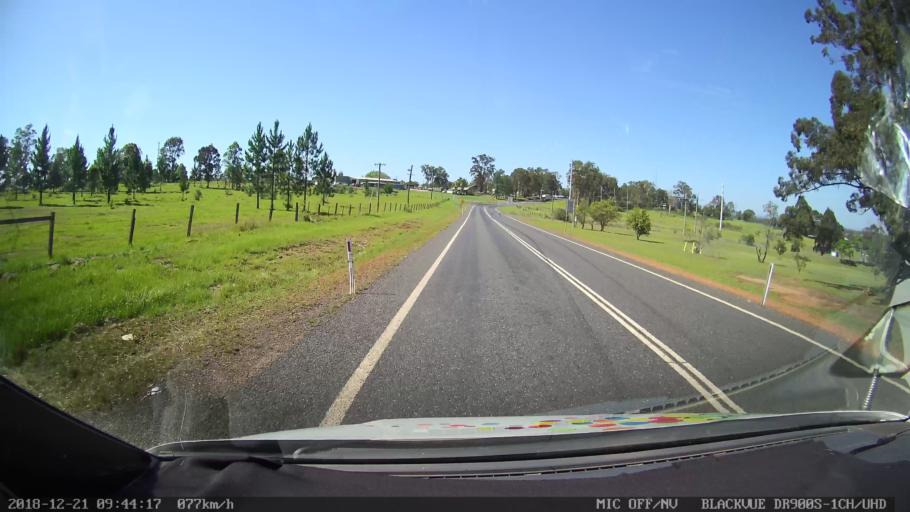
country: AU
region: New South Wales
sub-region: Clarence Valley
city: Grafton
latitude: -29.6163
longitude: 152.9341
